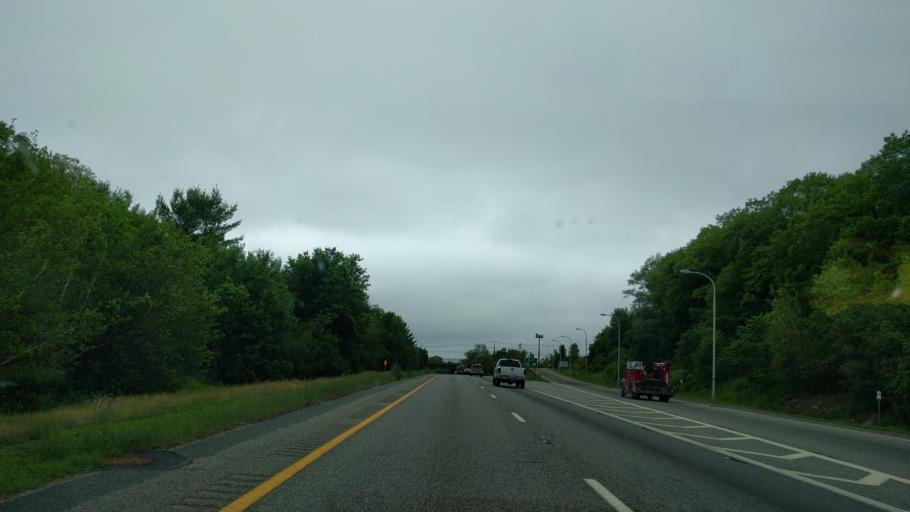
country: US
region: Rhode Island
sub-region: Providence County
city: Johnston
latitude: 41.8077
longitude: -71.5104
